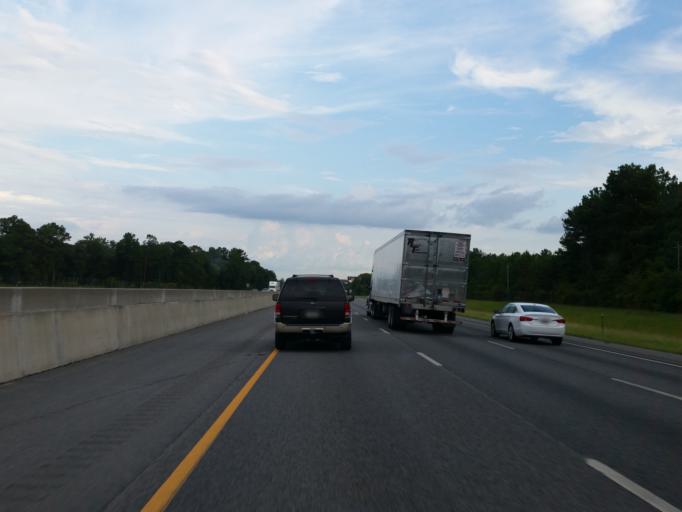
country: US
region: Georgia
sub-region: Lowndes County
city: Hahira
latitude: 31.0102
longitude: -83.3933
